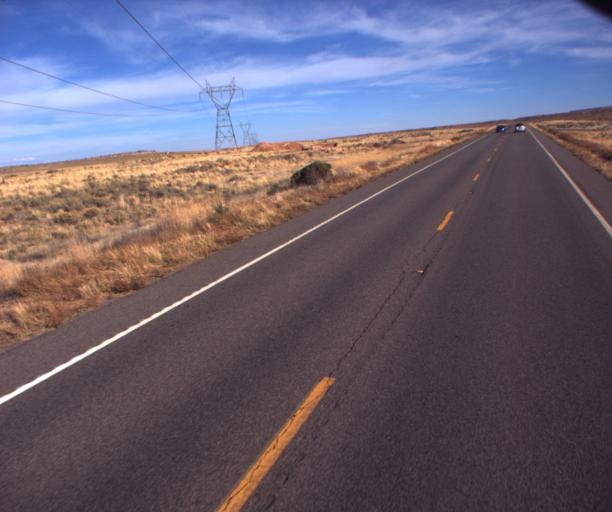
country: US
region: Arizona
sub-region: Apache County
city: Lukachukai
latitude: 36.9366
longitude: -109.2386
